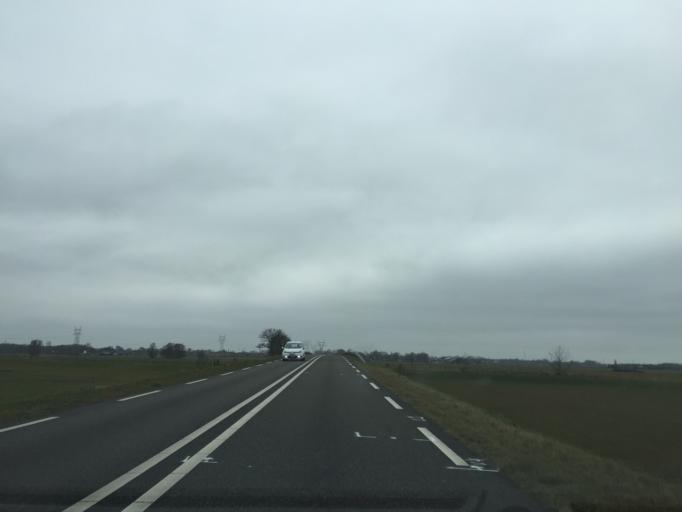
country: NL
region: South Holland
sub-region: Gemeente Leiderdorp
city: Leiderdorp
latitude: 52.1786
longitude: 4.5578
